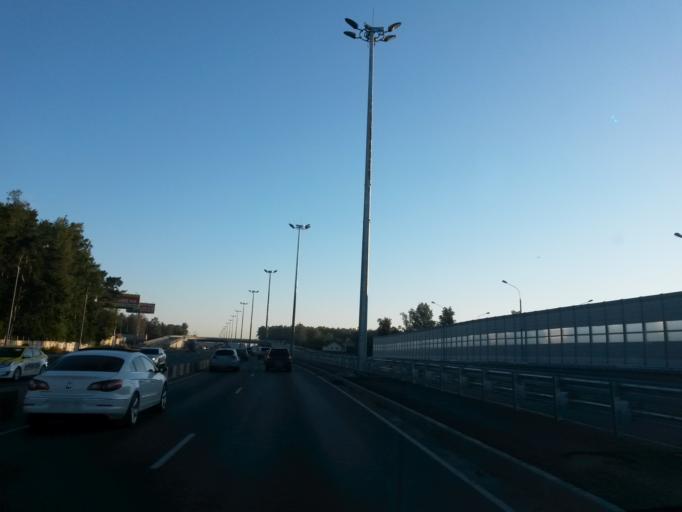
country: RU
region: Moskovskaya
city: Bolshevo
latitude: 55.9374
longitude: 37.8115
